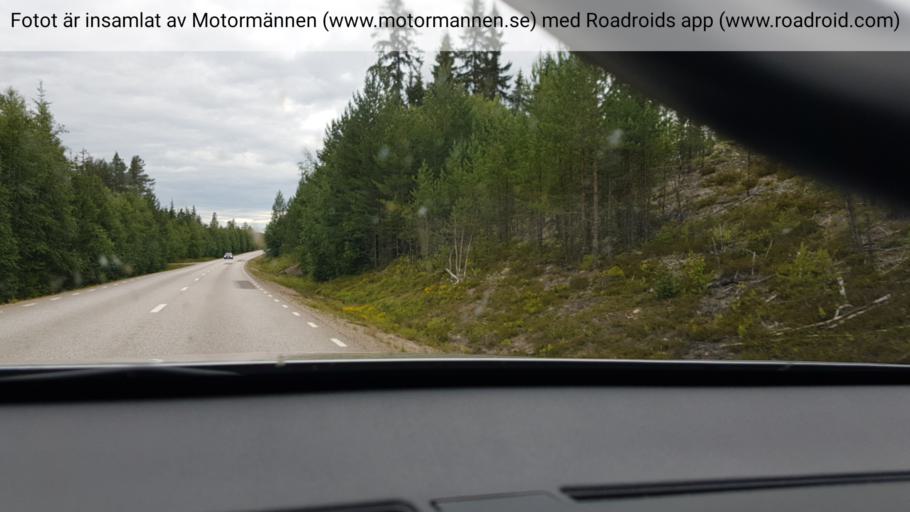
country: NO
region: Hedmark
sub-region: Trysil
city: Innbygda
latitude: 60.9351
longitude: 12.4834
